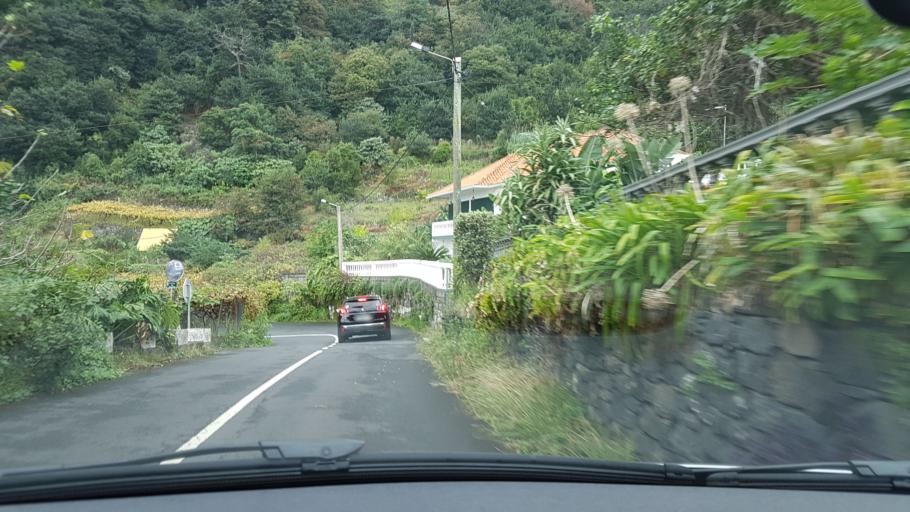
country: PT
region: Madeira
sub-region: Santana
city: Santana
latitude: 32.8241
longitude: -16.9559
